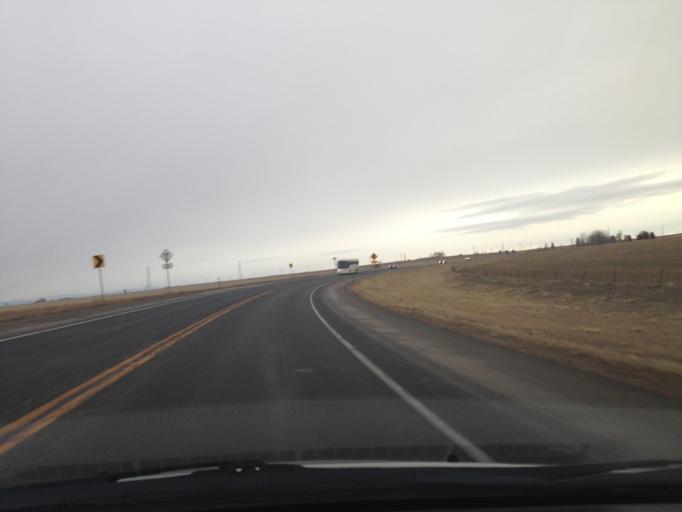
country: US
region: Colorado
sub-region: Weld County
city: Dacono
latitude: 40.0810
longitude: -104.9033
